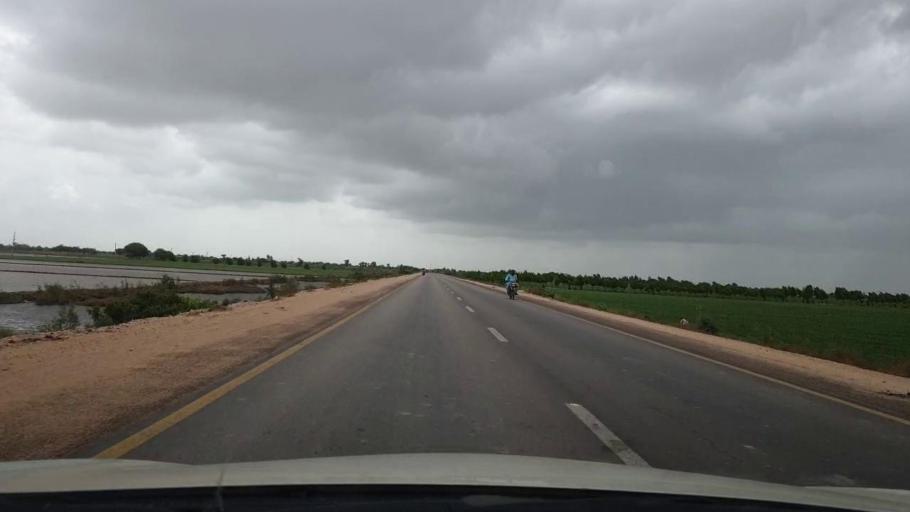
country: PK
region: Sindh
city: Mirpur Batoro
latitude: 24.6433
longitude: 68.4423
